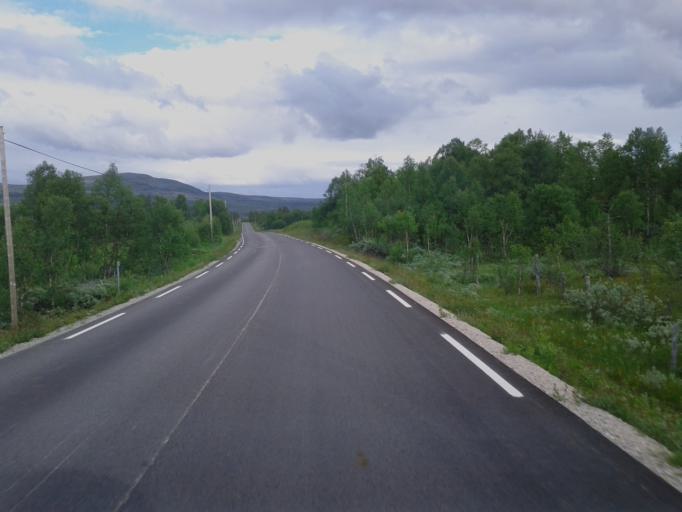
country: NO
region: Sor-Trondelag
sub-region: Roros
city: Roros
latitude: 62.3073
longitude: 11.6912
